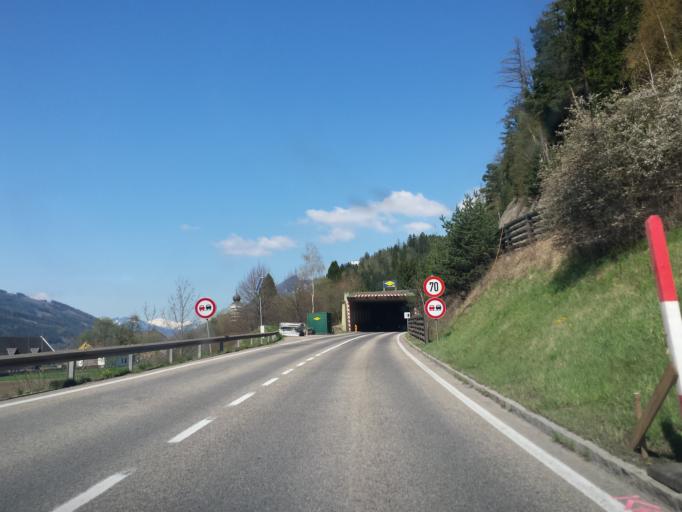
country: AT
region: Styria
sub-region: Politischer Bezirk Leoben
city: Traboch
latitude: 47.3766
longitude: 14.9908
